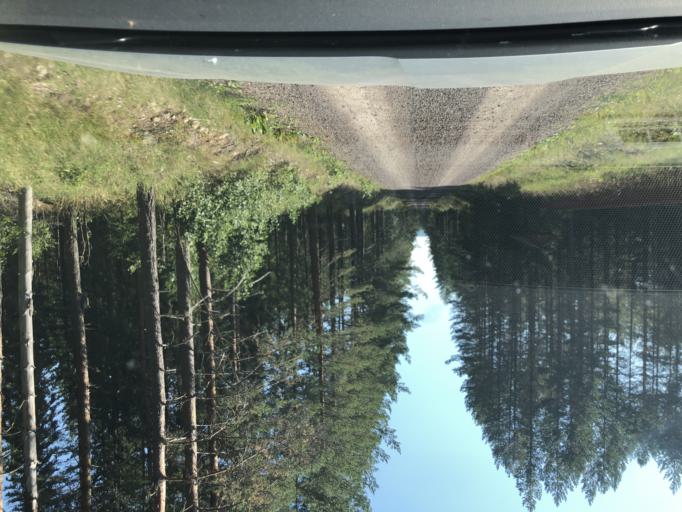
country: SE
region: Dalarna
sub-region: Orsa Kommun
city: Orsa
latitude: 61.2189
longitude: 14.7104
